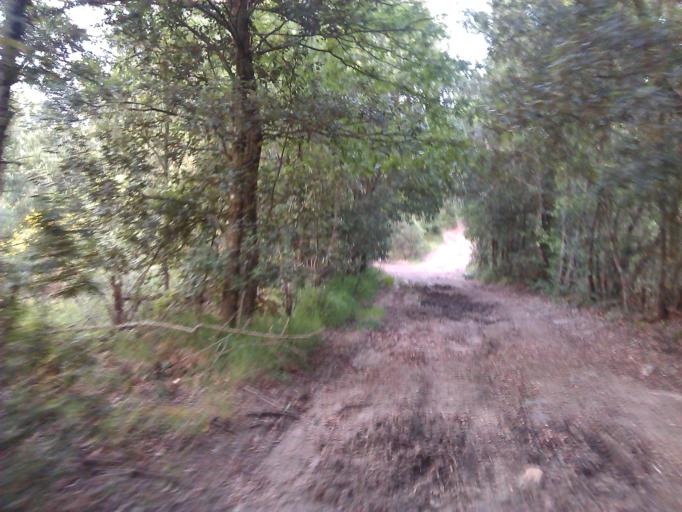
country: IT
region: Tuscany
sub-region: Province of Arezzo
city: Ponticino
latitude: 43.4590
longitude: 11.7412
